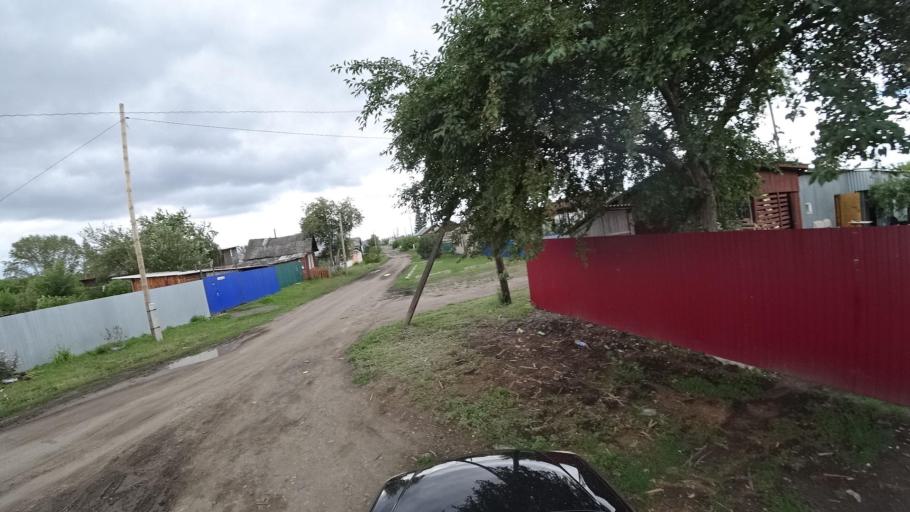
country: RU
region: Sverdlovsk
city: Kamyshlov
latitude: 56.8528
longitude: 62.6957
